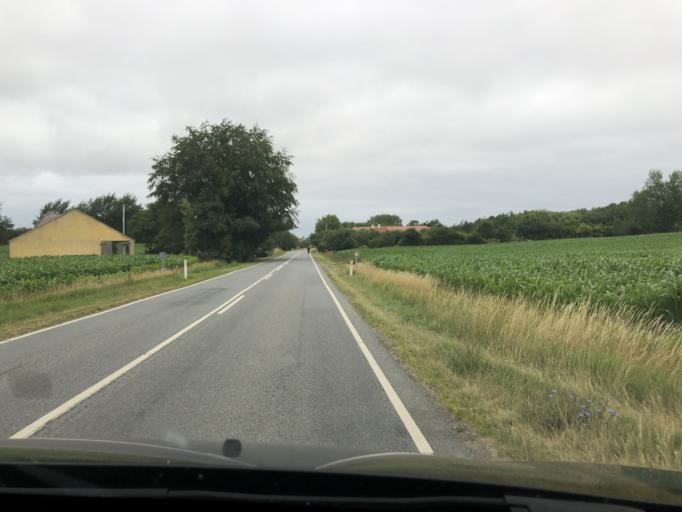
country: DK
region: South Denmark
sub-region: AEro Kommune
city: AEroskobing
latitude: 54.9008
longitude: 10.3015
